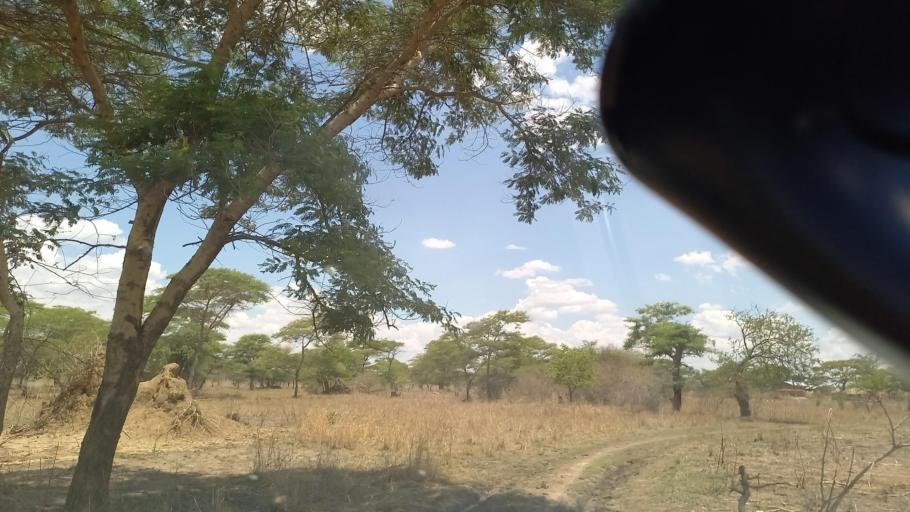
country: ZM
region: Southern
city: Mazabuka
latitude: -16.1242
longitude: 27.7787
